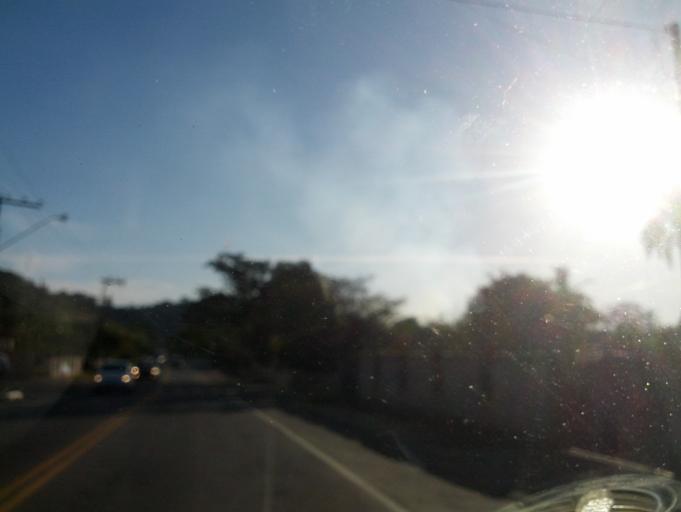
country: BR
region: Santa Catarina
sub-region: Indaial
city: Indaial
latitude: -26.8884
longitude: -49.2061
